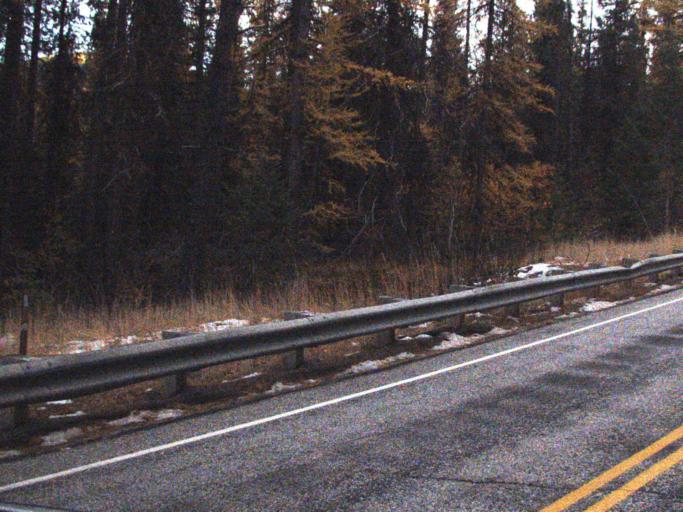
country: US
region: Washington
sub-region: Ferry County
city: Republic
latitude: 48.6238
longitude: -118.4449
